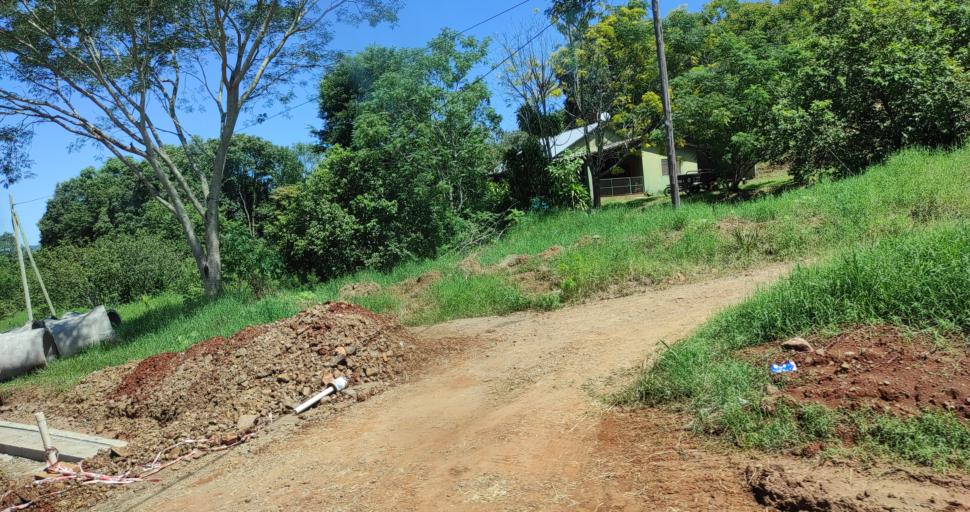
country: AR
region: Misiones
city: El Soberbio
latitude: -27.2892
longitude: -54.2090
